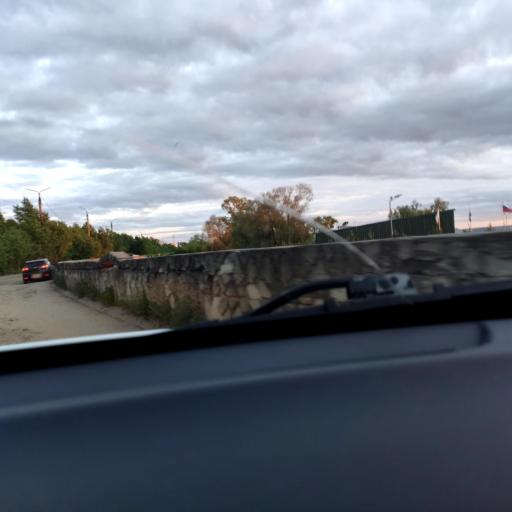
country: RU
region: Tatarstan
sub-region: Gorod Kazan'
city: Kazan
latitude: 55.7836
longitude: 49.0981
